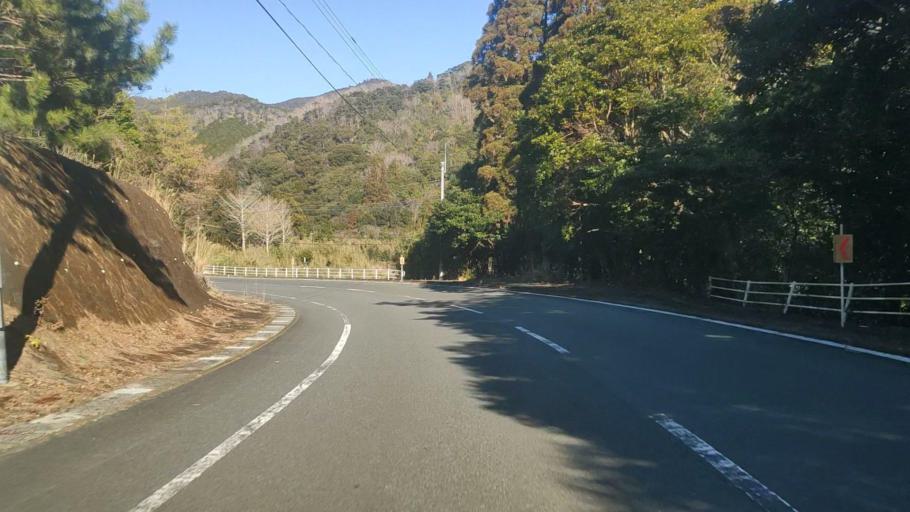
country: JP
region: Oita
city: Saiki
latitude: 32.7410
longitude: 131.8244
